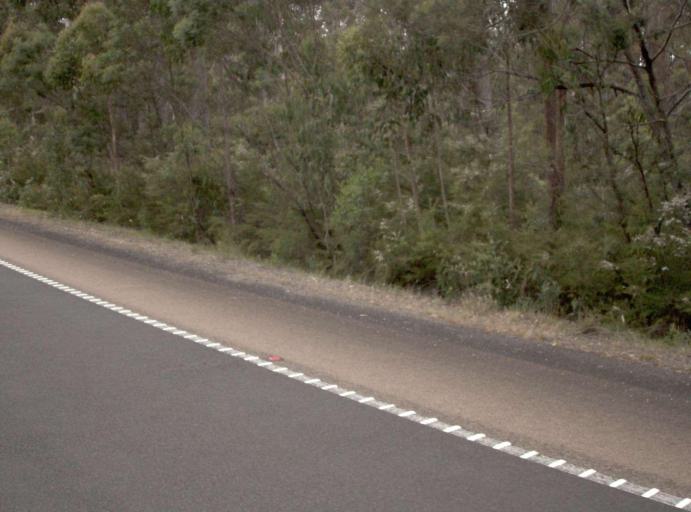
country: AU
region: Victoria
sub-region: East Gippsland
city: Lakes Entrance
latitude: -37.7164
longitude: 147.9608
